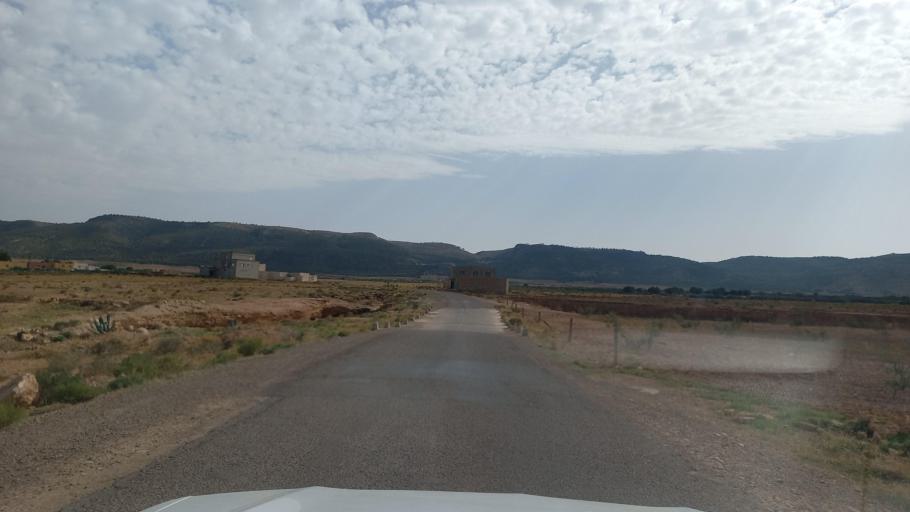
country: TN
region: Al Qasrayn
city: Kasserine
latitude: 35.3564
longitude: 8.8270
